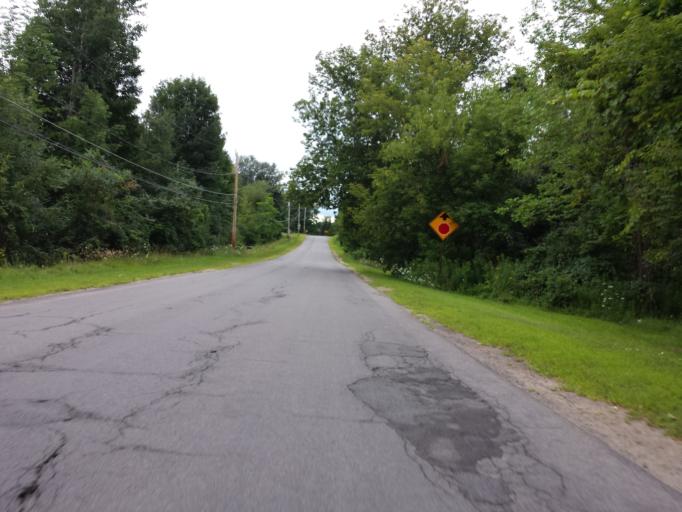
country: US
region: New York
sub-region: St. Lawrence County
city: Potsdam
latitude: 44.7063
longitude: -75.0076
